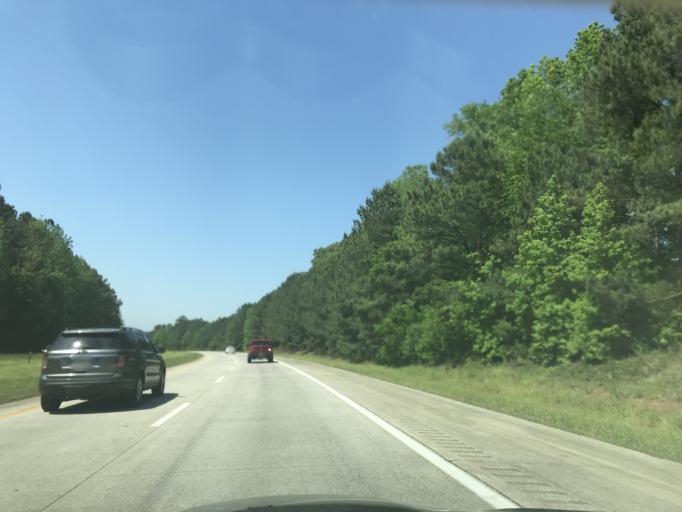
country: US
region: North Carolina
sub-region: Johnston County
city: Benson
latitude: 35.4522
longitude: -78.5336
